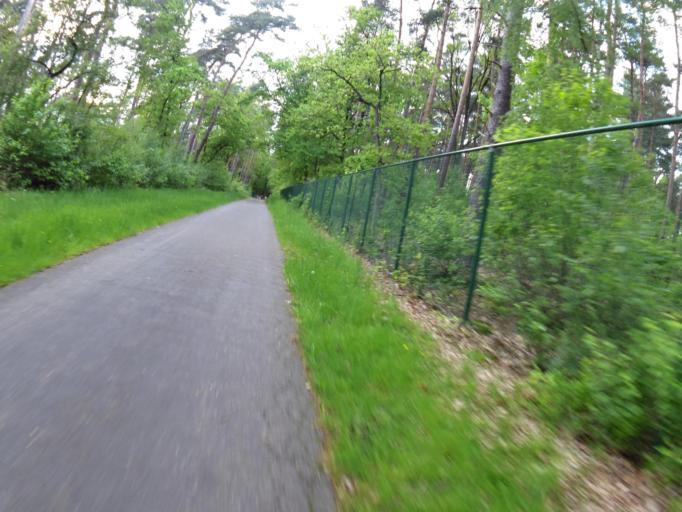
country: BE
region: Flanders
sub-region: Provincie Limburg
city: Genk
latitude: 50.9529
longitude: 5.5306
